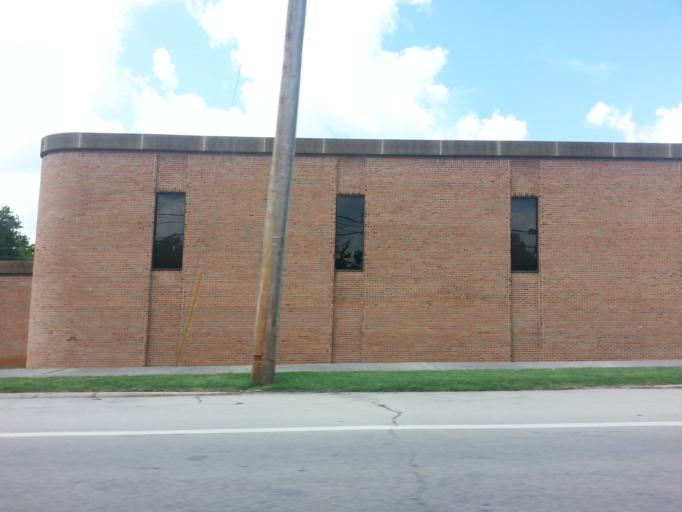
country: US
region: Tennessee
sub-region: Blount County
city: Alcoa
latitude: 35.7957
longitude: -83.9737
